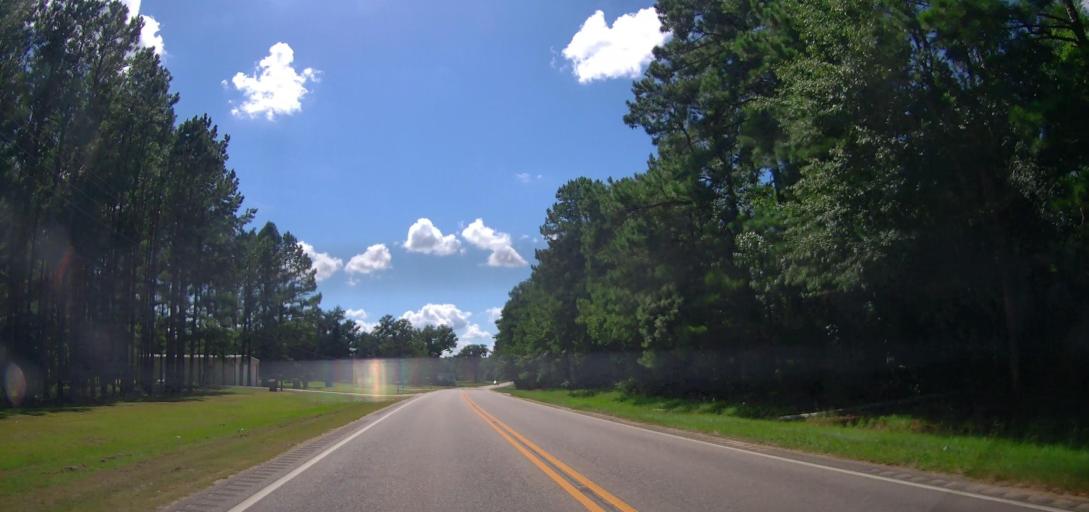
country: US
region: Alabama
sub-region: Macon County
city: Tuskegee
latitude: 32.3748
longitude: -85.8442
